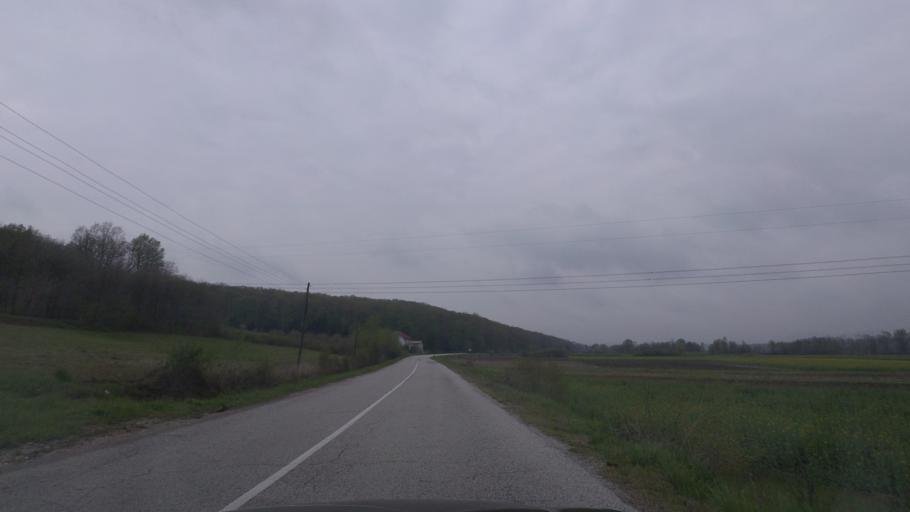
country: HR
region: Zagrebacka
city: Jastrebarsko
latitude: 45.6224
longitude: 15.5610
